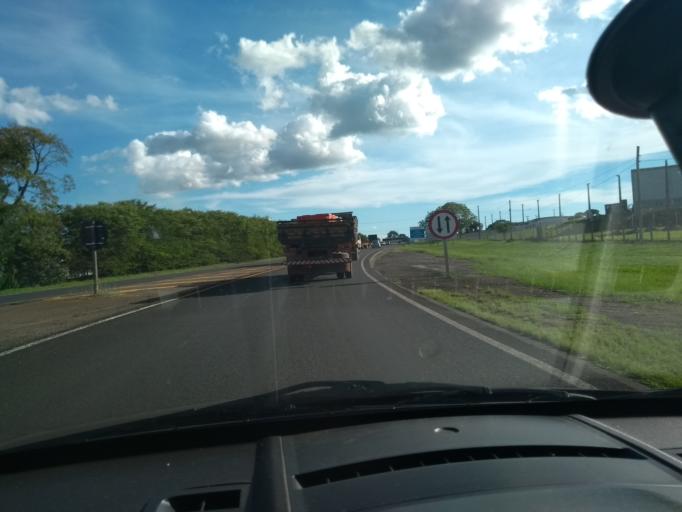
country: BR
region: Sao Paulo
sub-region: Casa Branca
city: Casa Branca
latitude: -21.7869
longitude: -47.0661
